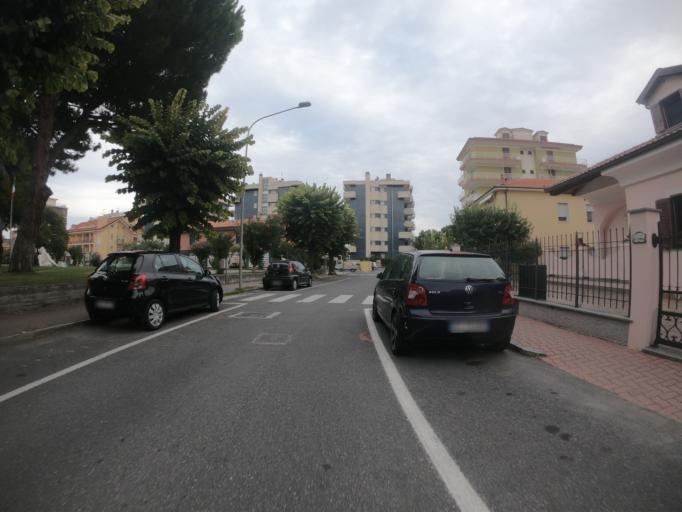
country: IT
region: Liguria
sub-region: Provincia di Savona
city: Marina di Andora
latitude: 43.9524
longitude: 8.1487
